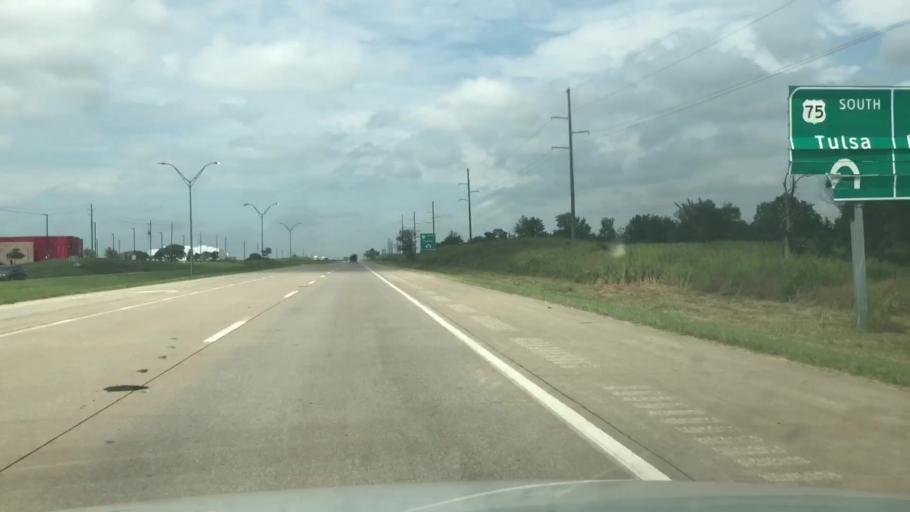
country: US
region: Oklahoma
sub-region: Washington County
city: Bartlesville
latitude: 36.5617
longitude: -95.9292
